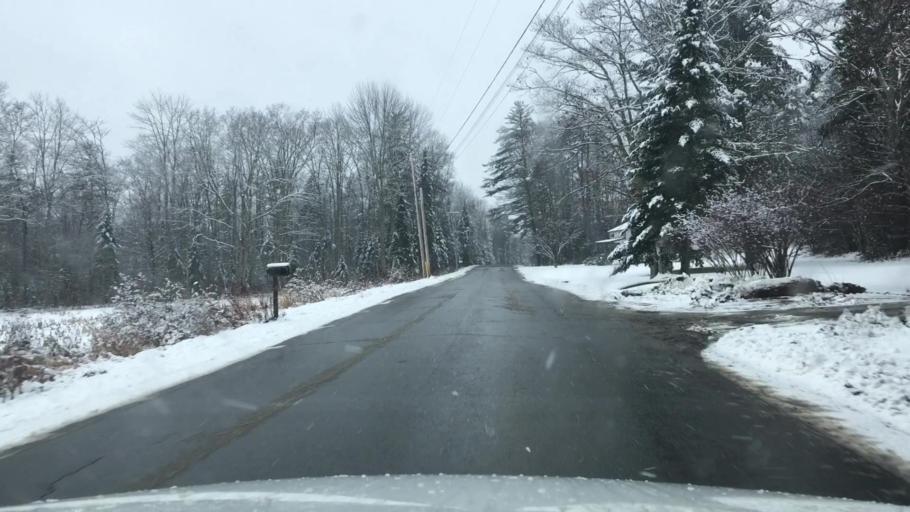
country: US
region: Maine
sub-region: Knox County
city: Union
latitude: 44.1708
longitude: -69.3260
